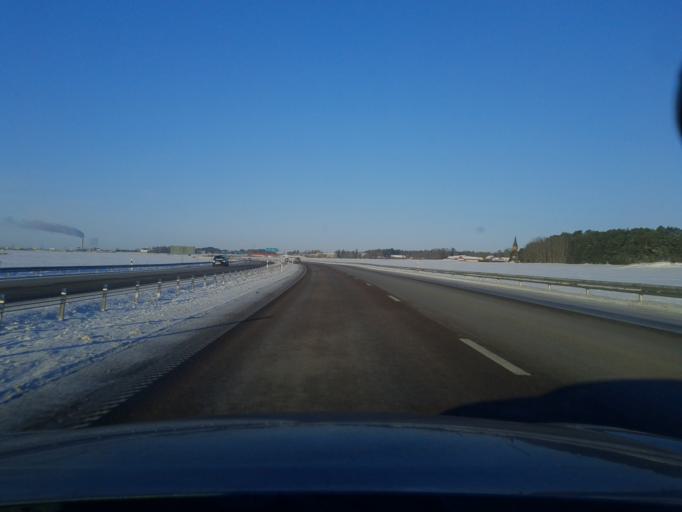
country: SE
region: Uppsala
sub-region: Uppsala Kommun
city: Saevja
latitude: 59.8212
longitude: 17.7509
